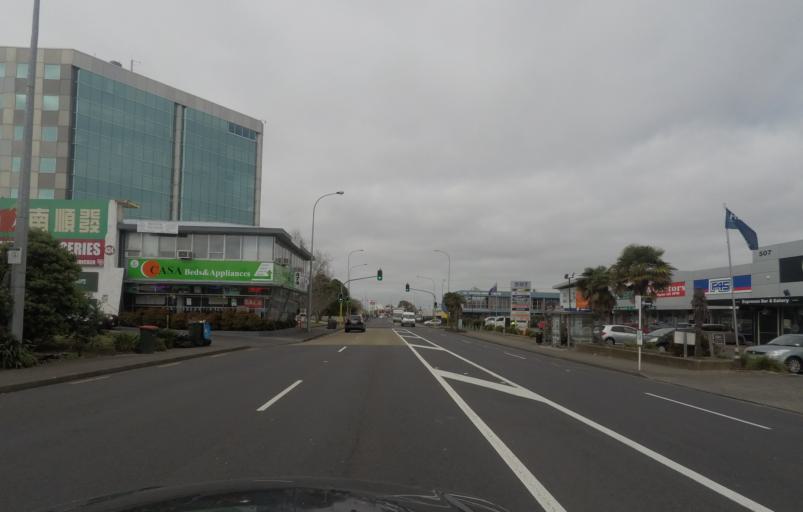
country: NZ
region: Auckland
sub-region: Auckland
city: Mangere
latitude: -36.9463
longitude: 174.8454
